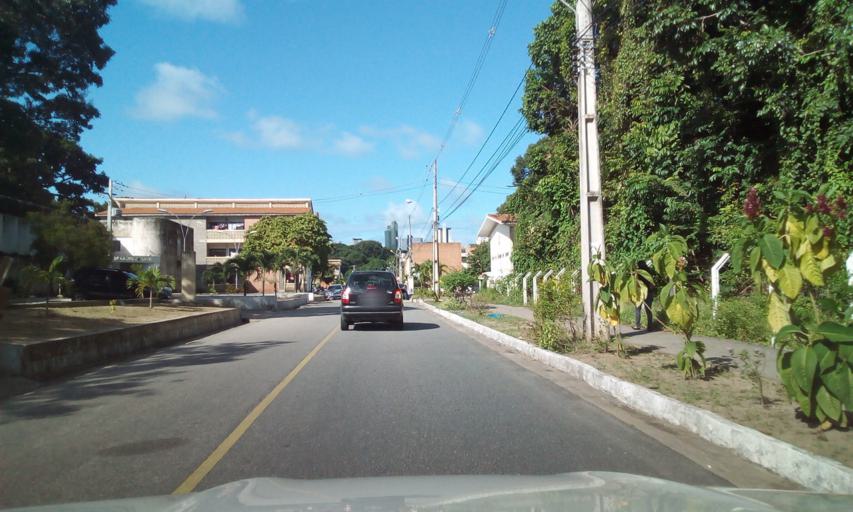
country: BR
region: Paraiba
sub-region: Joao Pessoa
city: Joao Pessoa
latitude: -7.1346
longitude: -34.8427
